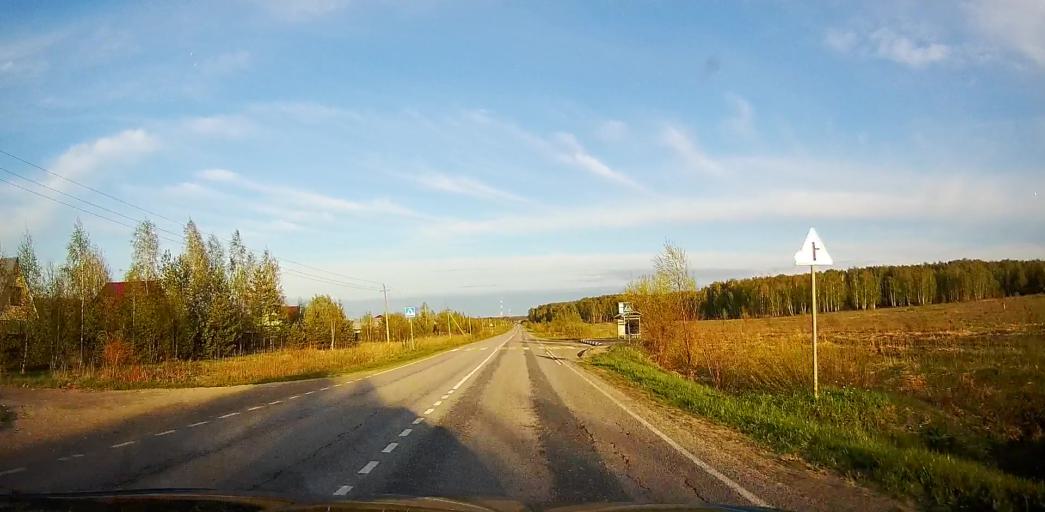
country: RU
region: Moskovskaya
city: Meshcherino
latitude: 55.2407
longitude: 38.3373
